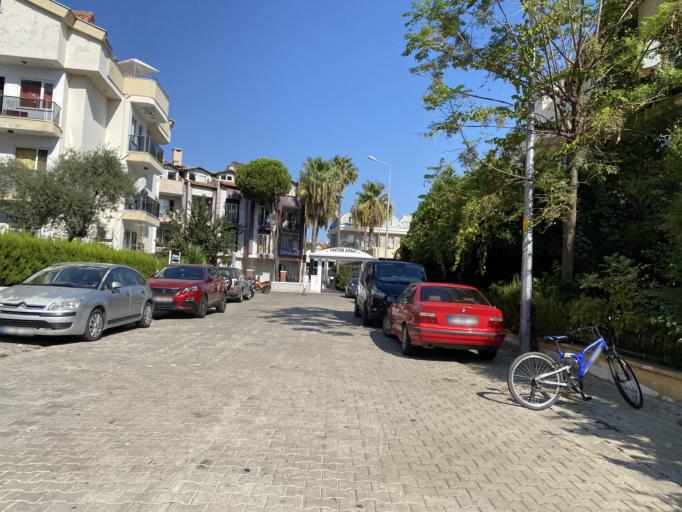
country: TR
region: Mugla
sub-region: Marmaris
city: Marmaris
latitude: 36.8449
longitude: 28.2520
